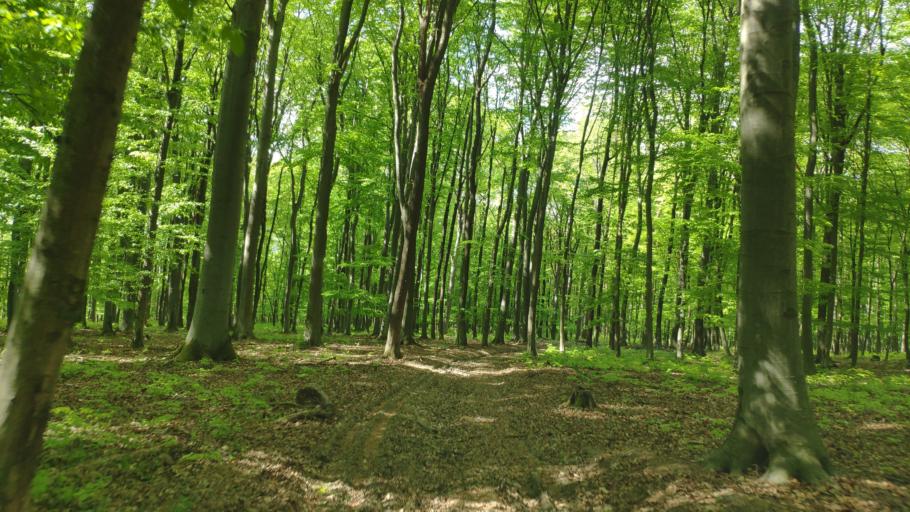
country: SK
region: Kosicky
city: Kosice
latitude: 48.6704
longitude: 21.4469
